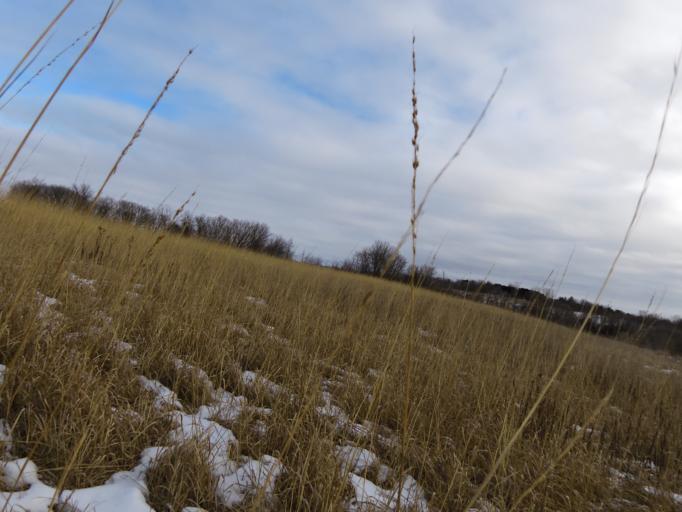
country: US
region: Wisconsin
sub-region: Pierce County
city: Prescott
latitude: 44.8016
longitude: -92.8274
